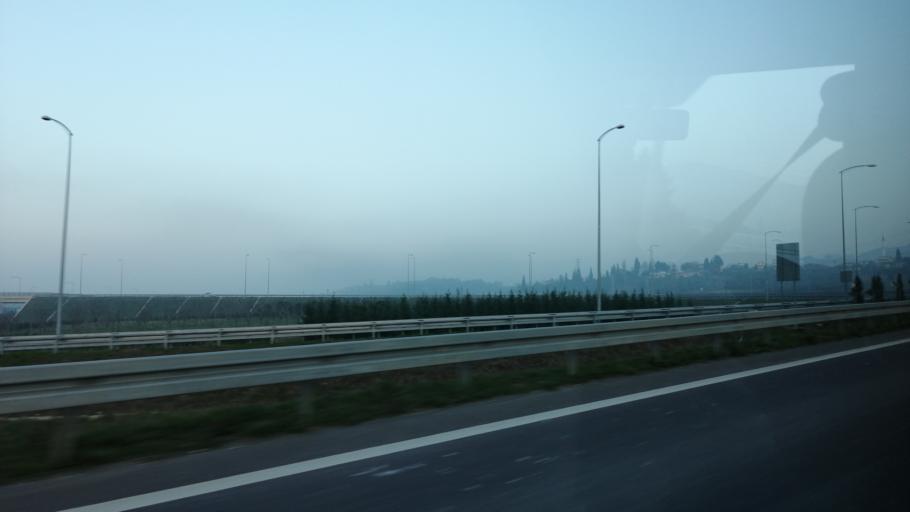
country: TR
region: Yalova
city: Altinova
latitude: 40.6895
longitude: 29.4684
